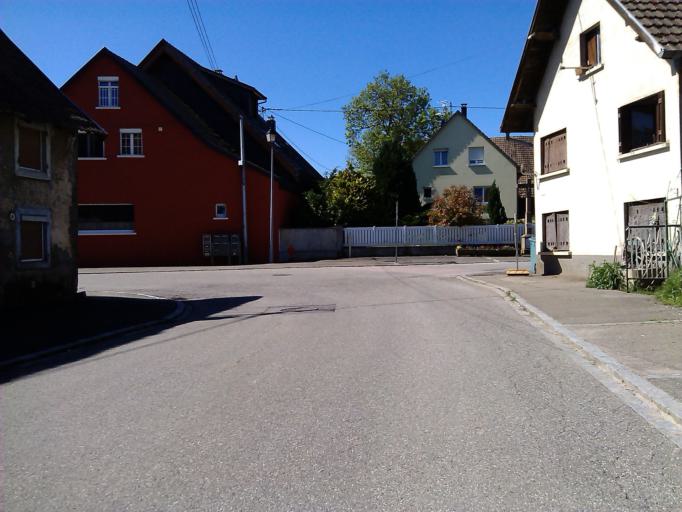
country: FR
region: Alsace
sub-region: Departement du Haut-Rhin
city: Dannemarie
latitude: 47.6334
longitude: 7.0928
